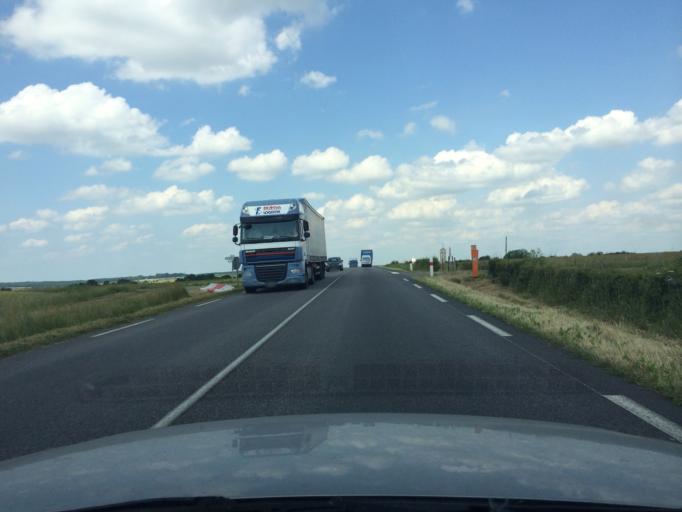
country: FR
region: Lorraine
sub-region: Departement de la Moselle
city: Lorquin
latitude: 48.6743
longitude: 6.9474
